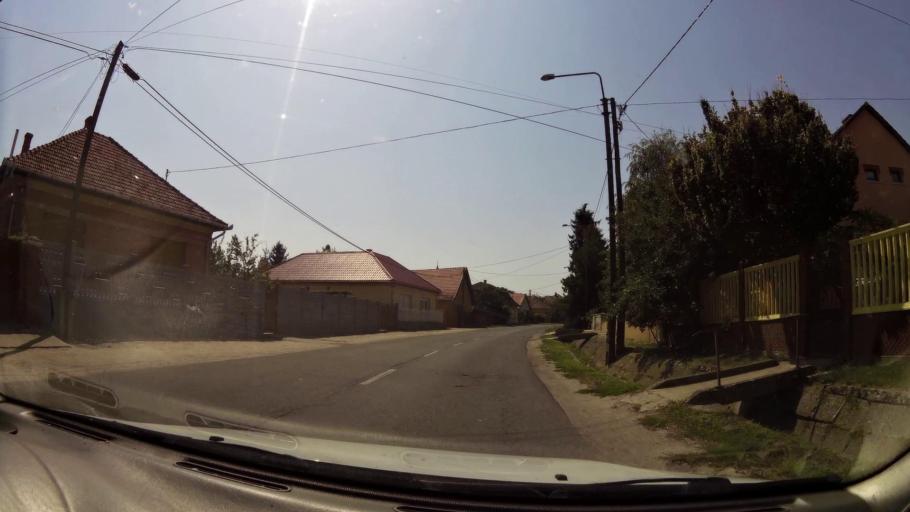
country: HU
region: Pest
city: Tapioszentmarton
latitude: 47.3433
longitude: 19.7455
